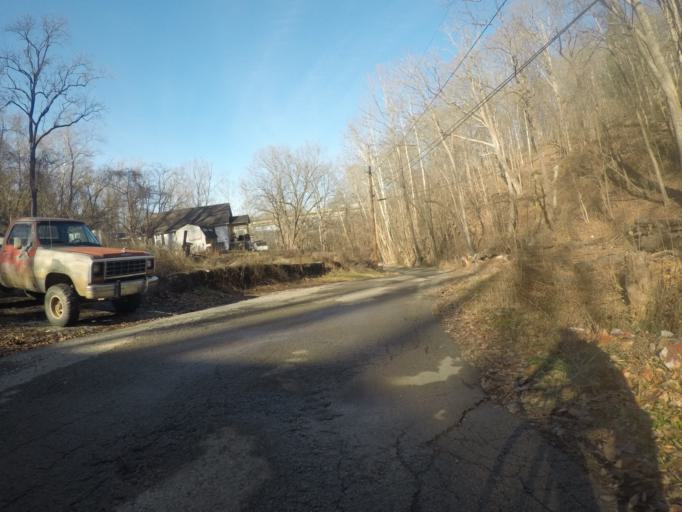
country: US
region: Ohio
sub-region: Lawrence County
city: Burlington
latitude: 38.3957
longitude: -82.4991
